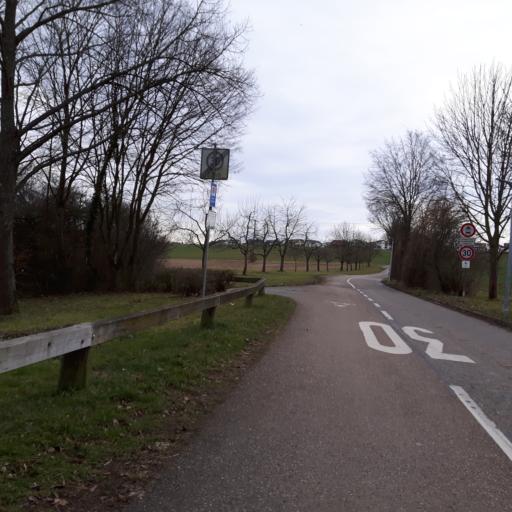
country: DE
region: Baden-Wuerttemberg
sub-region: Regierungsbezirk Stuttgart
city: Steinheim am der Murr
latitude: 48.9779
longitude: 9.2849
